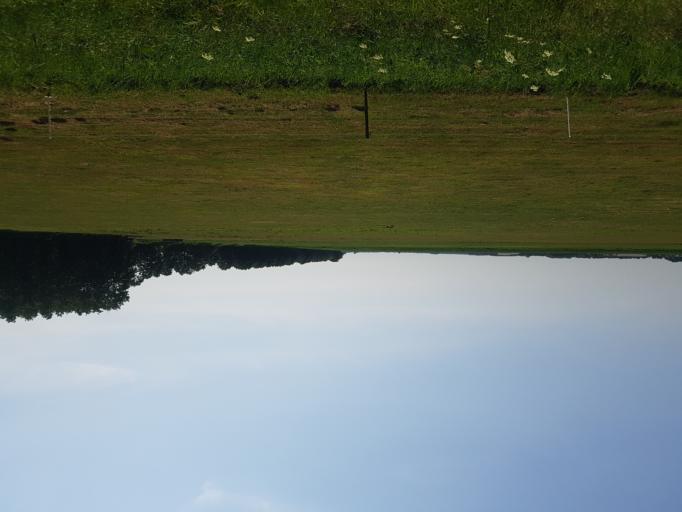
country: NL
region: Overijssel
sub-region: Gemeente Steenwijkerland
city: Tuk
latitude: 52.7717
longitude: 6.0896
